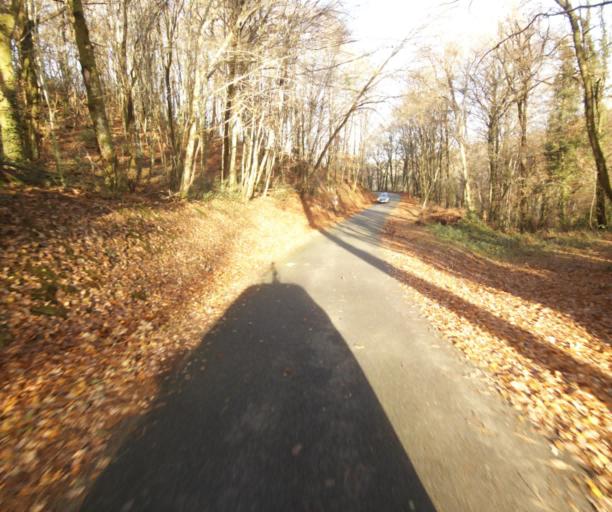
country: FR
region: Limousin
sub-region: Departement de la Correze
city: Laguenne
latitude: 45.2619
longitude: 1.8021
